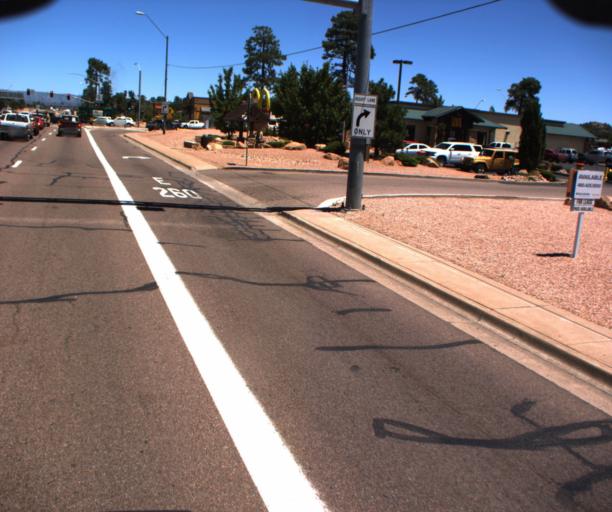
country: US
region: Arizona
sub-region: Gila County
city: Payson
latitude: 34.2396
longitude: -111.3229
